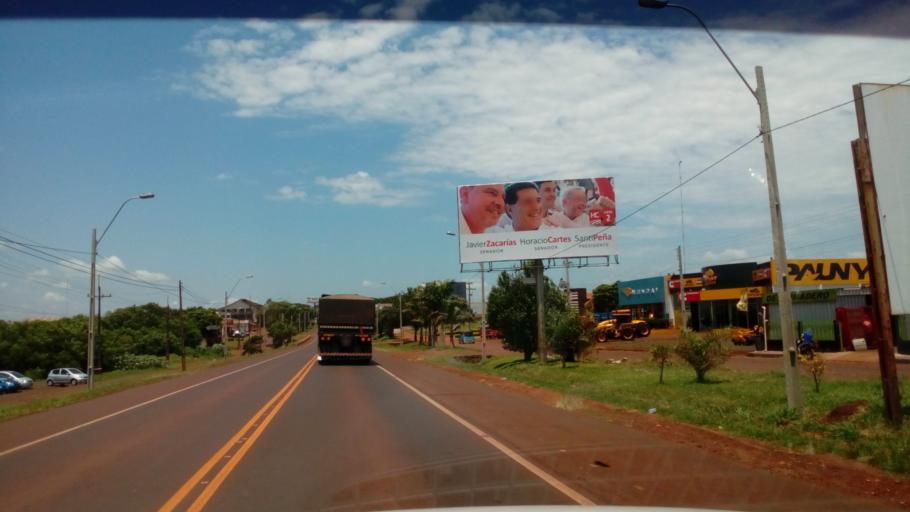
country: PY
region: Alto Parana
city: Santa Rita
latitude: -25.8109
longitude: -55.1031
